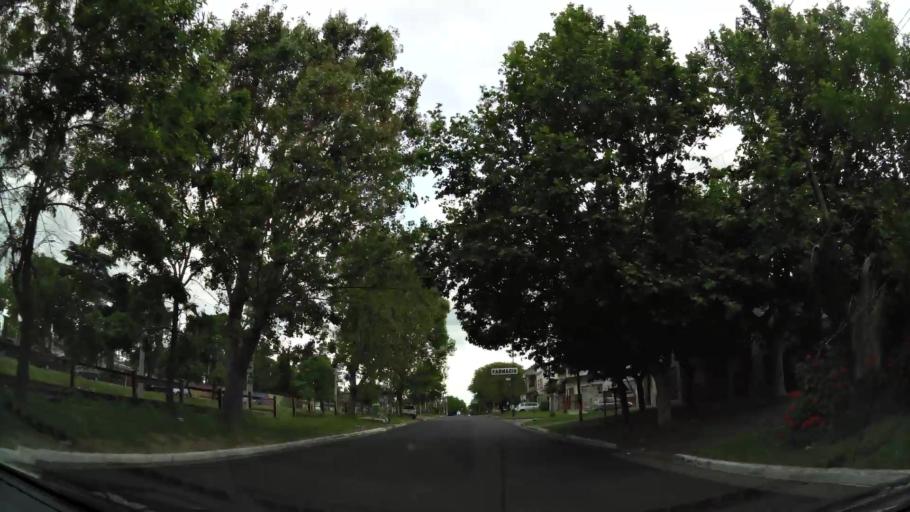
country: AR
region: Buenos Aires
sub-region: Partido de Quilmes
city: Quilmes
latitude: -34.7361
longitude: -58.2505
